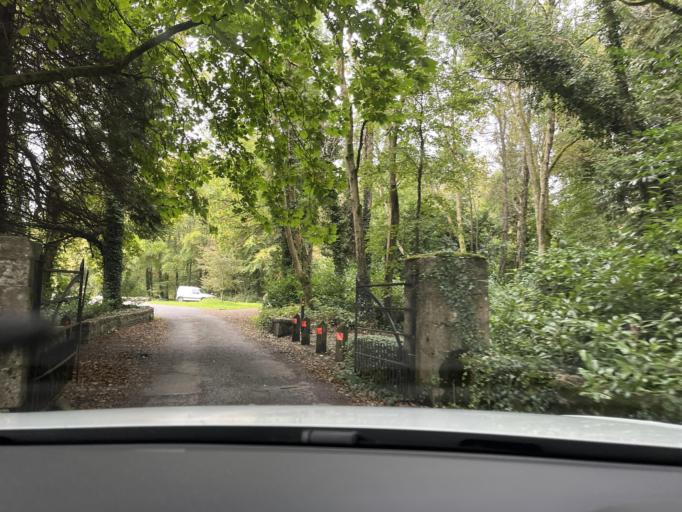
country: IE
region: Connaught
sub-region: Roscommon
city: Boyle
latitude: 53.9829
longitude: -8.2291
